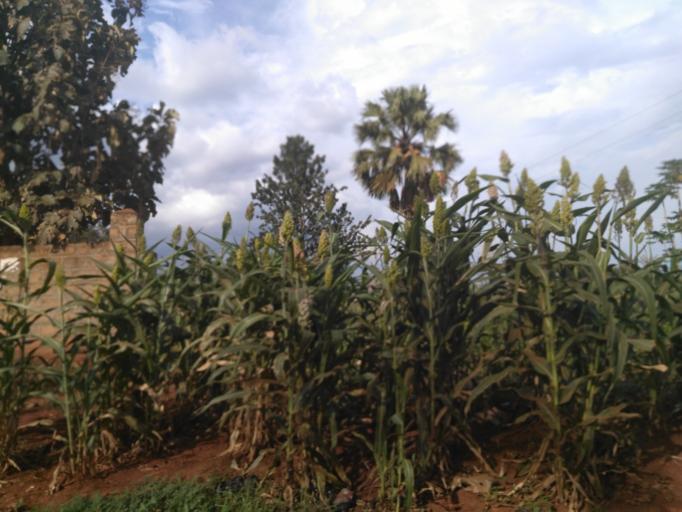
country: UG
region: Eastern Region
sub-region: Jinja District
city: Jinja
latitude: 0.4205
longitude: 33.2118
